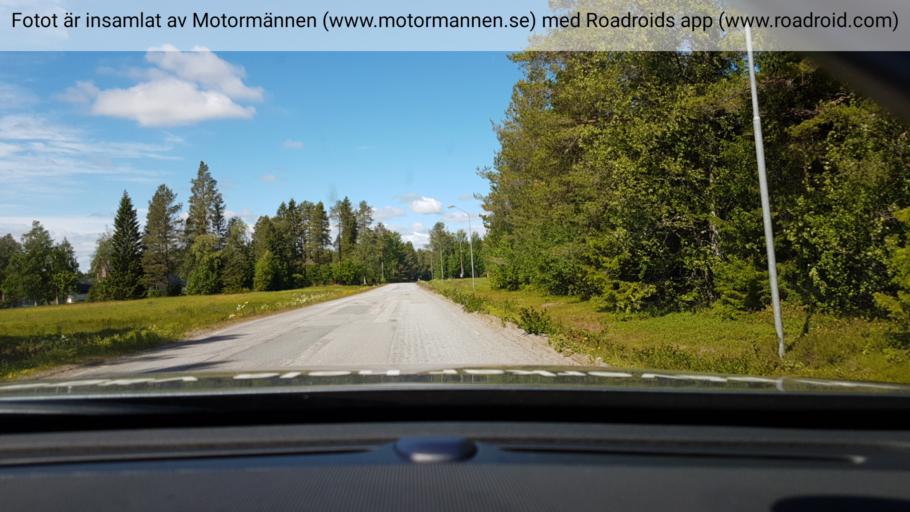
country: SE
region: Vaesterbotten
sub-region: Skelleftea Kommun
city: Burea
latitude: 64.4616
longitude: 21.4078
